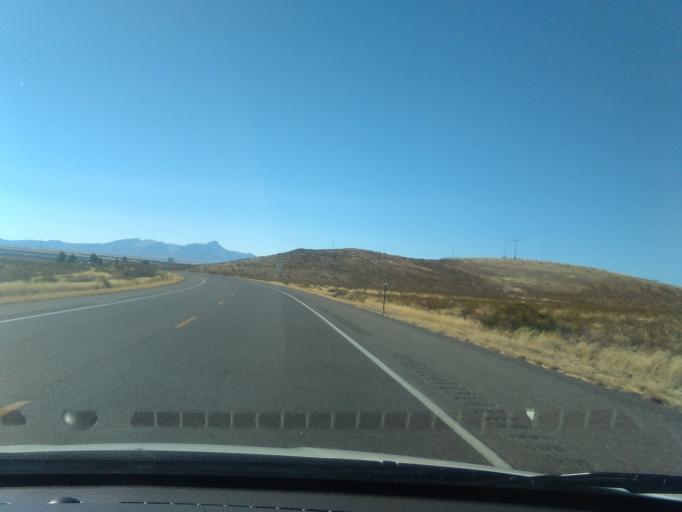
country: US
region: New Mexico
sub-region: Dona Ana County
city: Hatch
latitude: 32.5780
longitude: -107.4453
